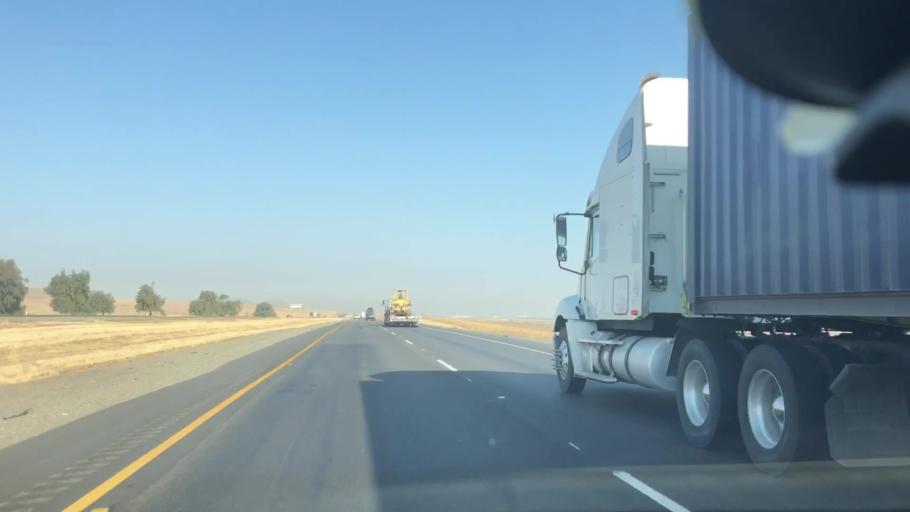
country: US
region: California
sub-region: San Joaquin County
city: Tracy
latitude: 37.6776
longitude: -121.4657
